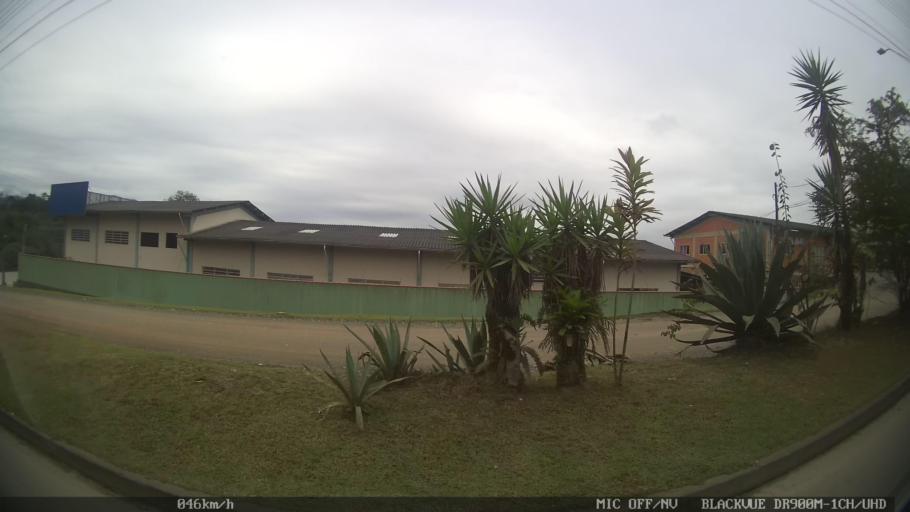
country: BR
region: Santa Catarina
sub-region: Joinville
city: Joinville
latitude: -26.2741
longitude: -48.8906
